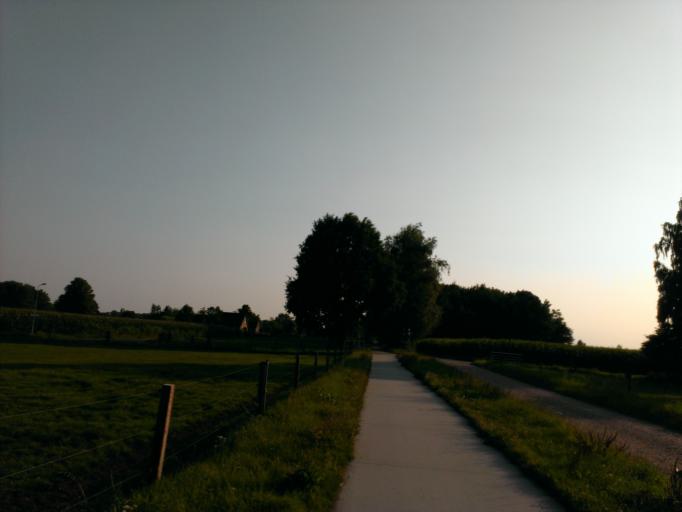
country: NL
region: Gelderland
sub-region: Gemeente Heerde
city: Heerde
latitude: 52.4097
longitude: 6.0589
